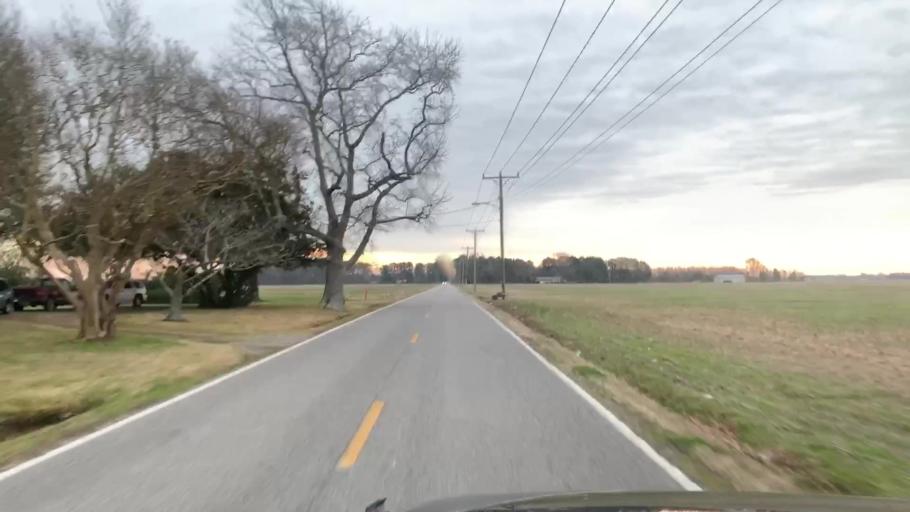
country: US
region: North Carolina
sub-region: Currituck County
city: Moyock
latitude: 36.6342
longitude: -76.1868
